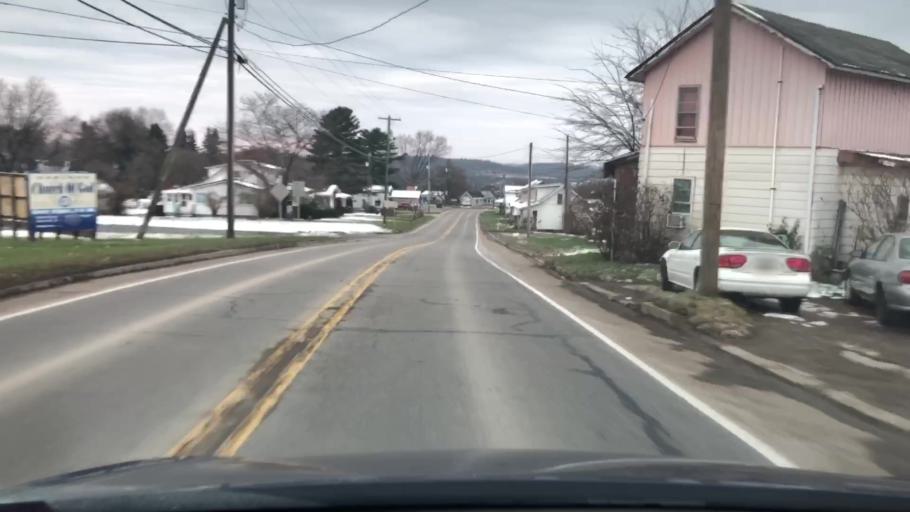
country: US
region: Pennsylvania
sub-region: Armstrong County
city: Kittanning
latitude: 40.9725
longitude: -79.3515
